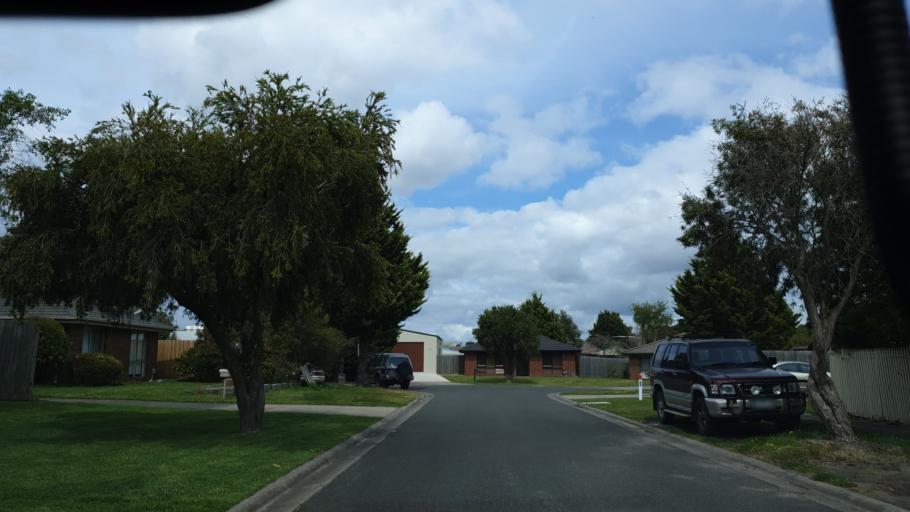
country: AU
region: Victoria
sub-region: Casey
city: Cranbourne North
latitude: -38.0792
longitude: 145.2789
